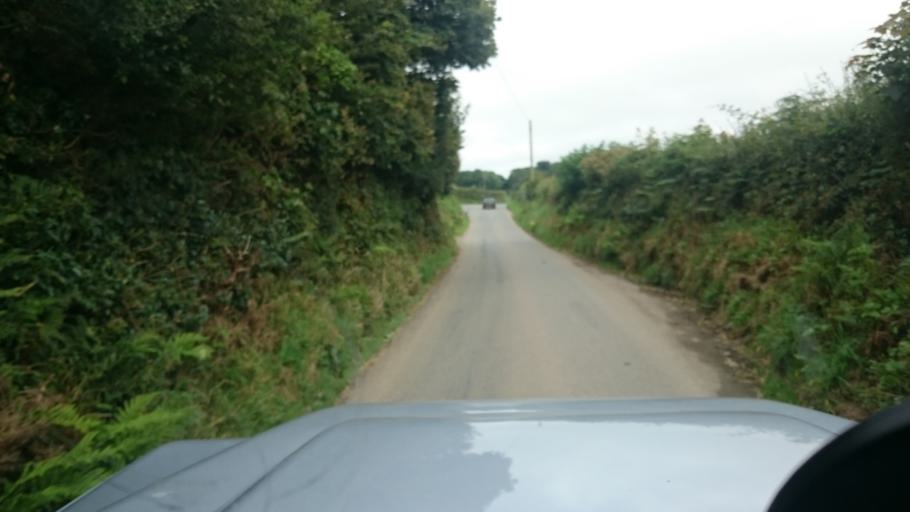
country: GB
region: Wales
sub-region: Pembrokeshire
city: Scleddau
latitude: 51.9268
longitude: -4.9575
